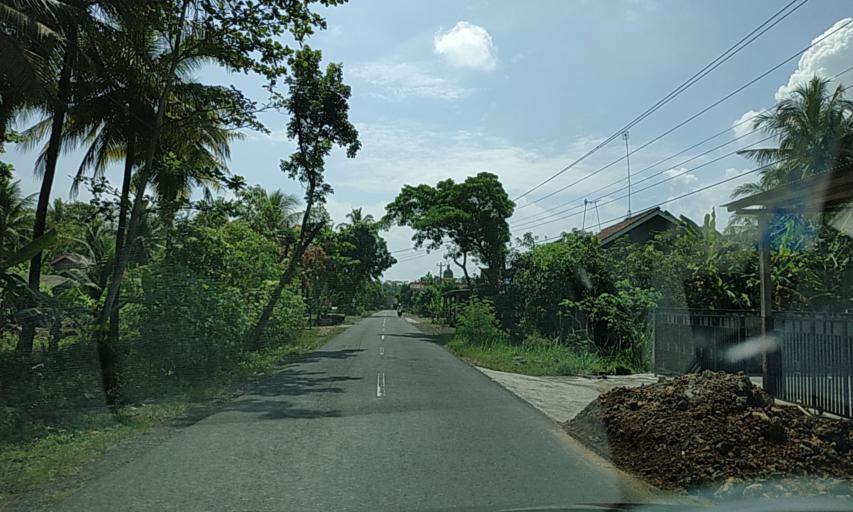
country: ID
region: Central Java
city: Kedungbulu
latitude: -7.5232
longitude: 108.7847
